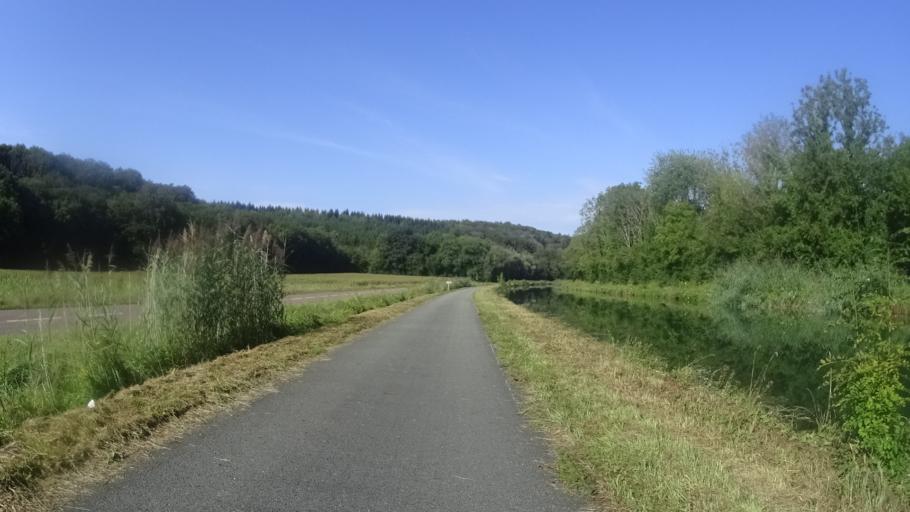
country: FR
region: Franche-Comte
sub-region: Departement du Doubs
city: Colombier-Fontaine
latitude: 47.4269
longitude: 6.6265
